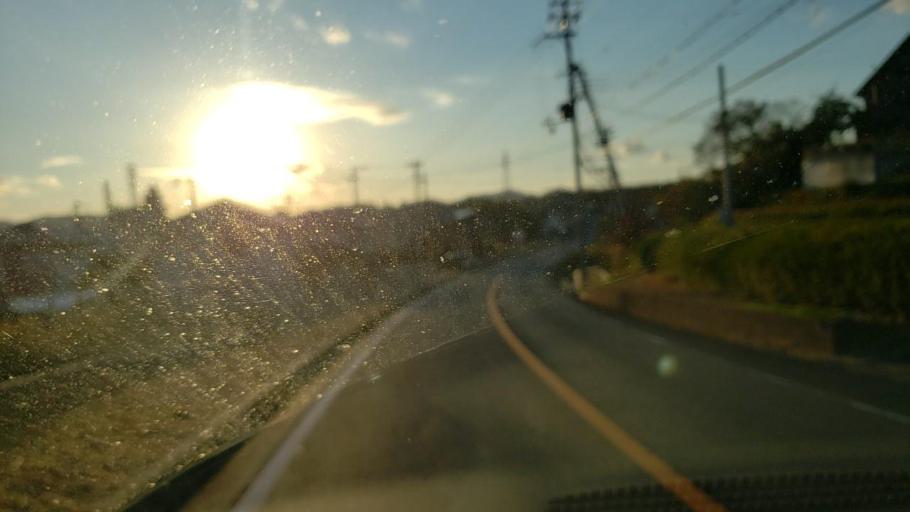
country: JP
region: Hyogo
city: Sumoto
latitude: 34.4408
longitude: 134.8969
